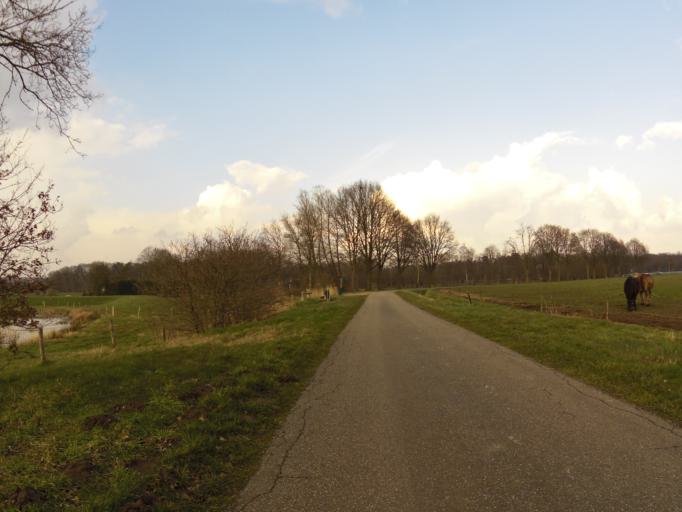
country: NL
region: North Brabant
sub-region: Gemeente Vught
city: Vught
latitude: 51.6264
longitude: 5.3100
